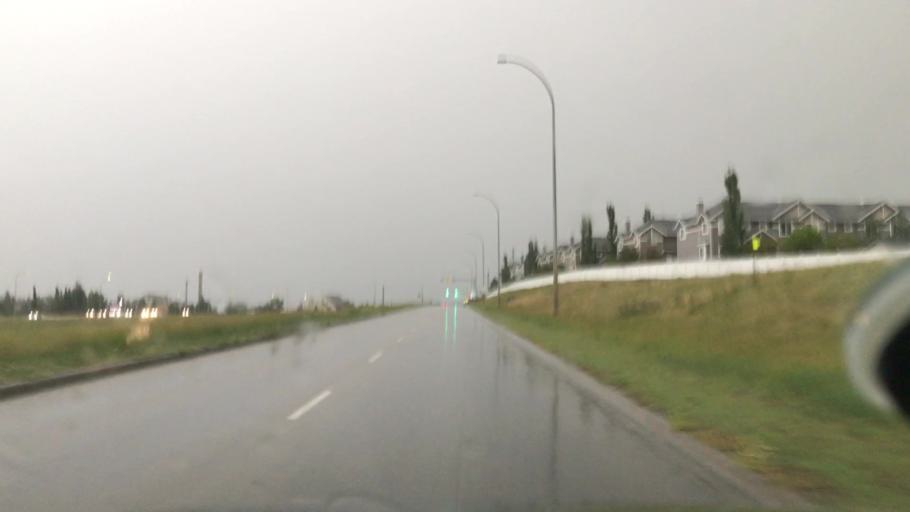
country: CA
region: Alberta
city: Edmonton
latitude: 53.4542
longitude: -113.5890
